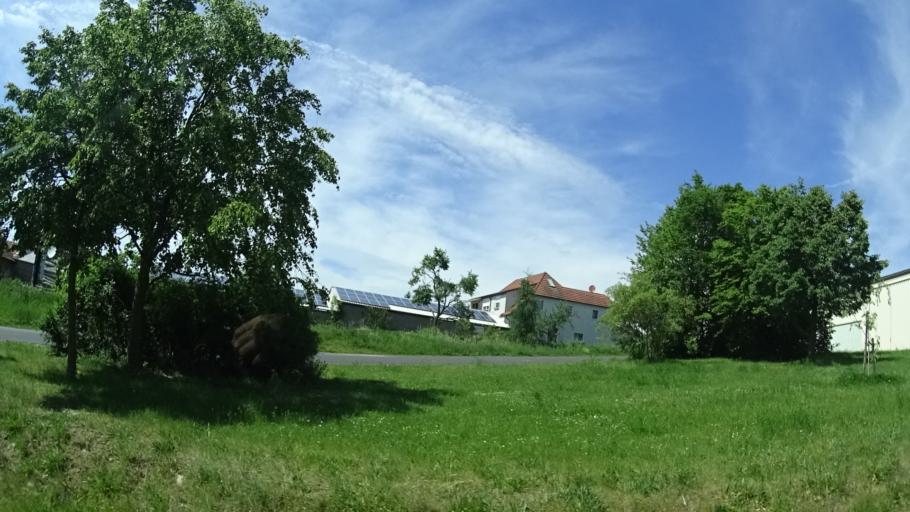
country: DE
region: Bavaria
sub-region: Regierungsbezirk Unterfranken
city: Wasserlosen
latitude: 50.0777
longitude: 10.0406
